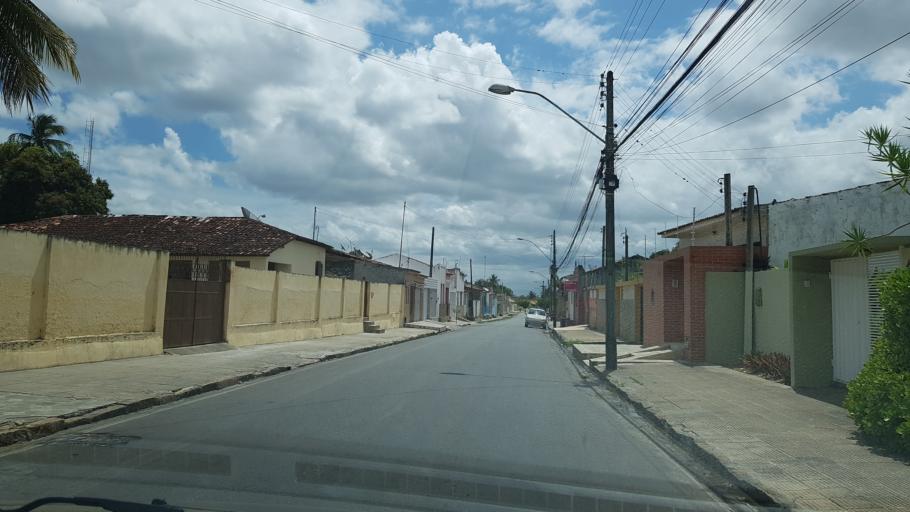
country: BR
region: Alagoas
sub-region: Penedo
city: Penedo
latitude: -10.2792
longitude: -36.5654
